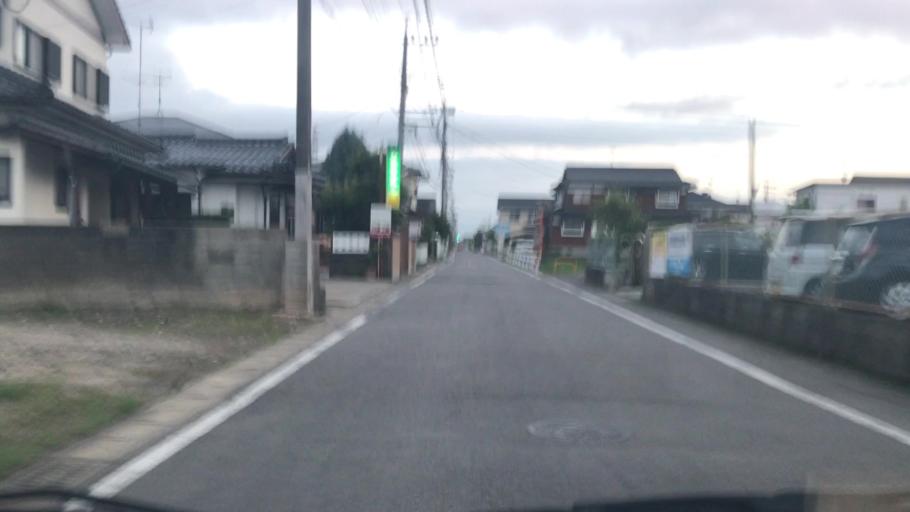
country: JP
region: Saga Prefecture
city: Saga-shi
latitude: 33.2328
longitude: 130.3017
